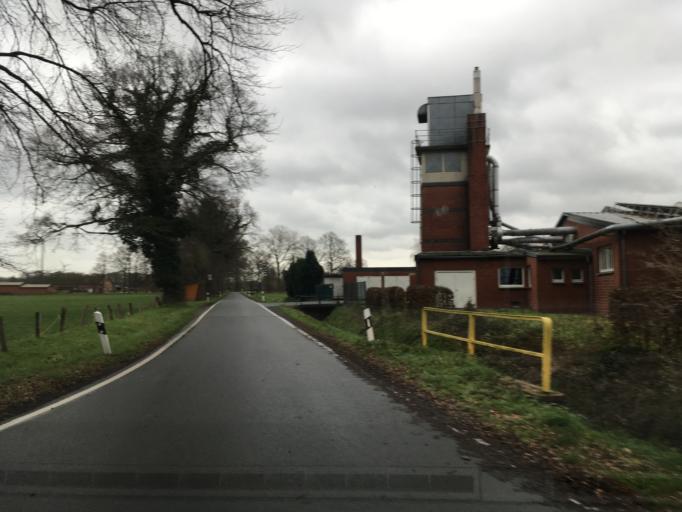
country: DE
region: North Rhine-Westphalia
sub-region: Regierungsbezirk Munster
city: Legden
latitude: 52.0590
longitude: 7.1060
